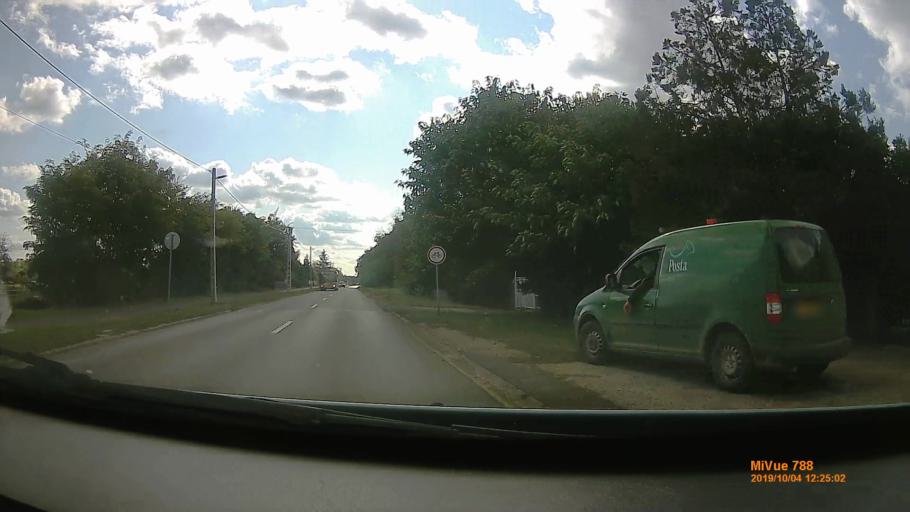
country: HU
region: Szabolcs-Szatmar-Bereg
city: Nyiregyhaza
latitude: 47.9903
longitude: 21.7040
